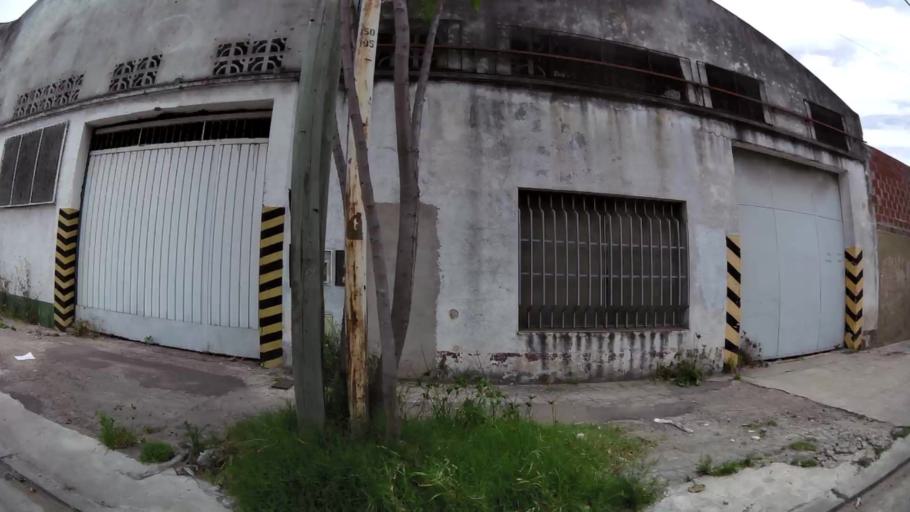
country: AR
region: Buenos Aires
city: San Justo
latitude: -34.6750
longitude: -58.5459
